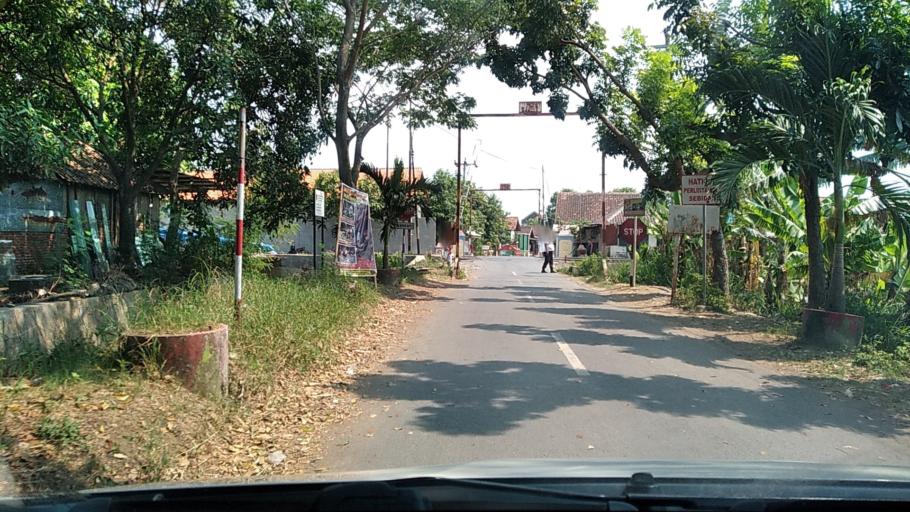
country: ID
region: Central Java
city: Semarang
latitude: -6.9753
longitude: 110.3437
